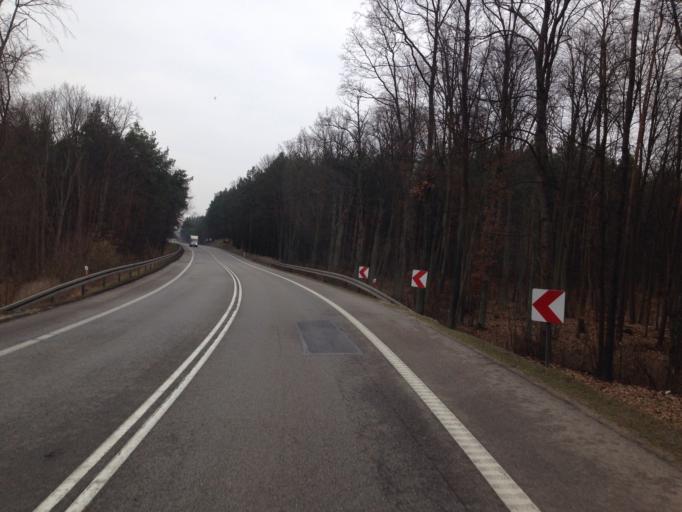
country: PL
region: Pomeranian Voivodeship
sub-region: Powiat starogardzki
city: Smetowo Graniczne
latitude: 53.7539
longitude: 18.7603
